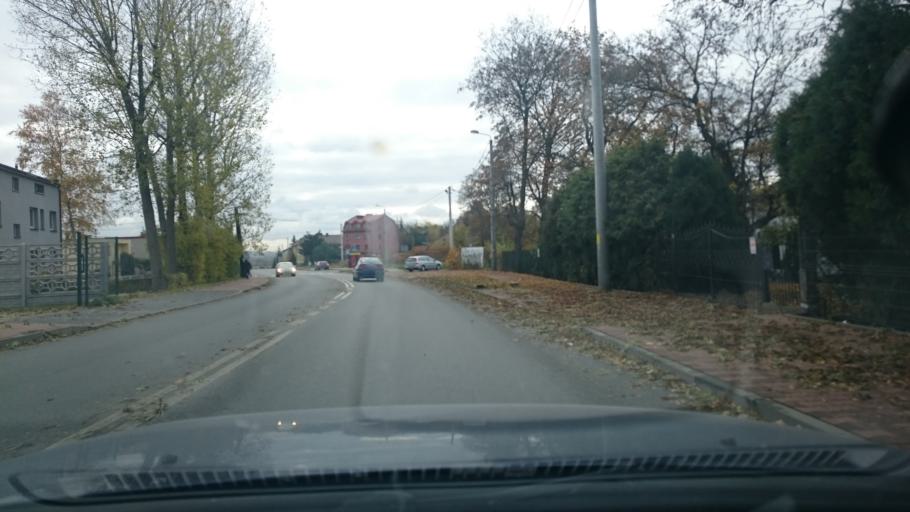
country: PL
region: Silesian Voivodeship
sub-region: Powiat bedzinski
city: Bedzin
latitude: 50.3458
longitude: 19.1003
